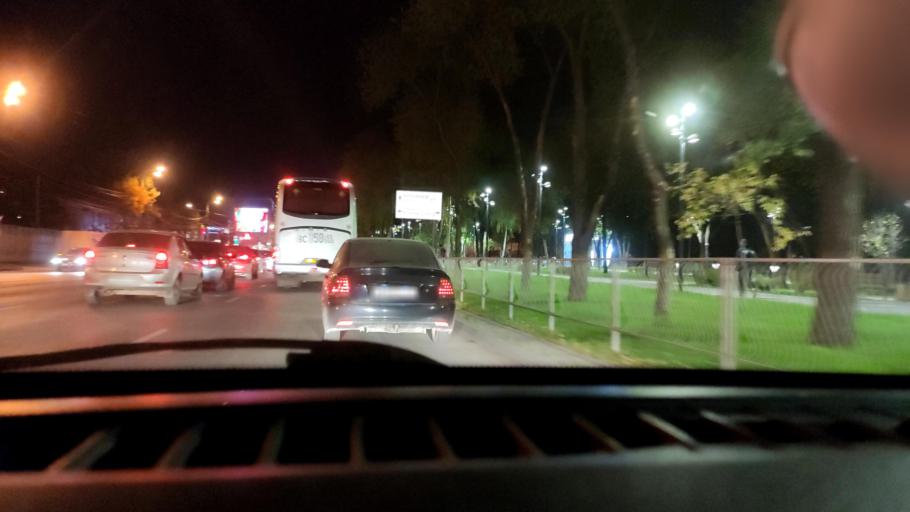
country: RU
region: Samara
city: Samara
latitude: 53.1955
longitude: 50.1907
